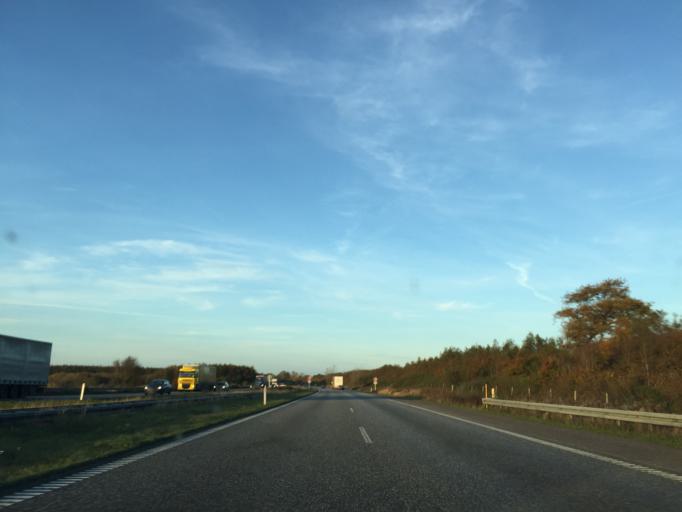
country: DK
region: South Denmark
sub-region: Kolding Kommune
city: Christiansfeld
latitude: 55.4010
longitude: 9.4519
